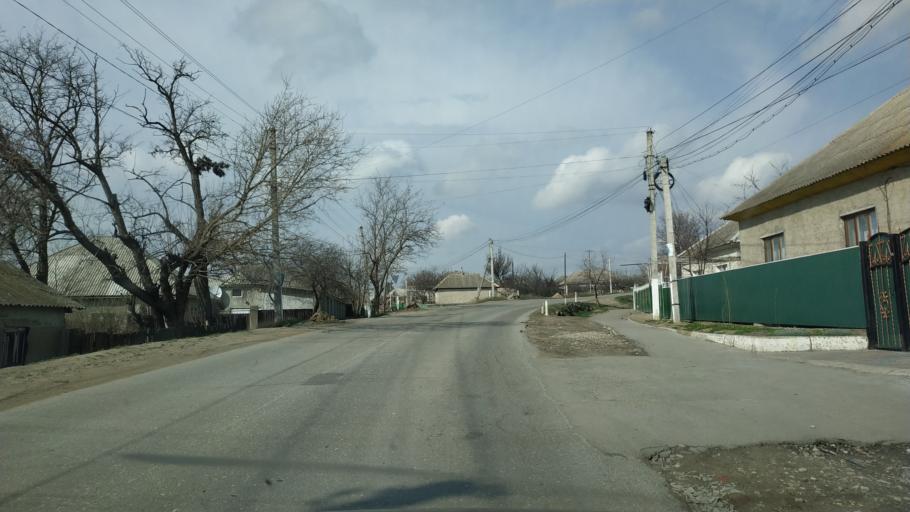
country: MD
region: Gagauzia
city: Vulcanesti
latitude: 45.6915
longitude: 28.4050
